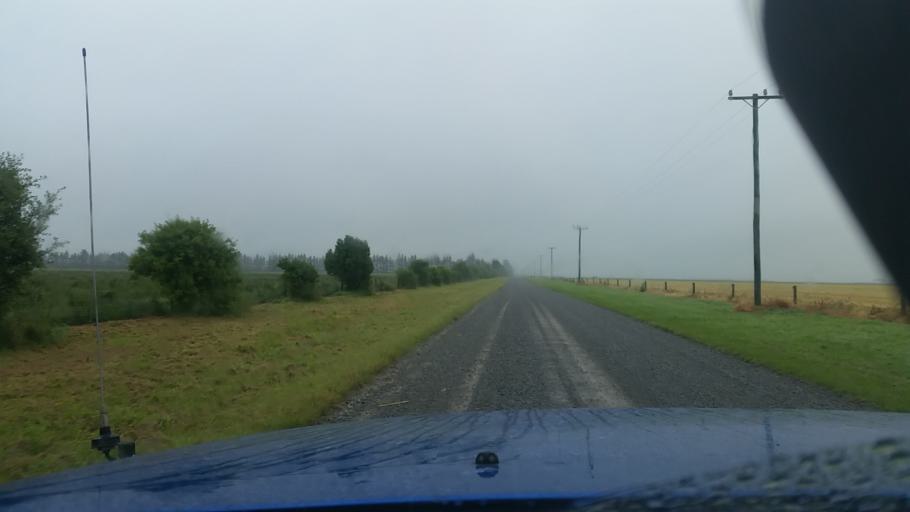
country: NZ
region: Canterbury
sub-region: Ashburton District
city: Rakaia
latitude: -43.7239
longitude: 171.8621
